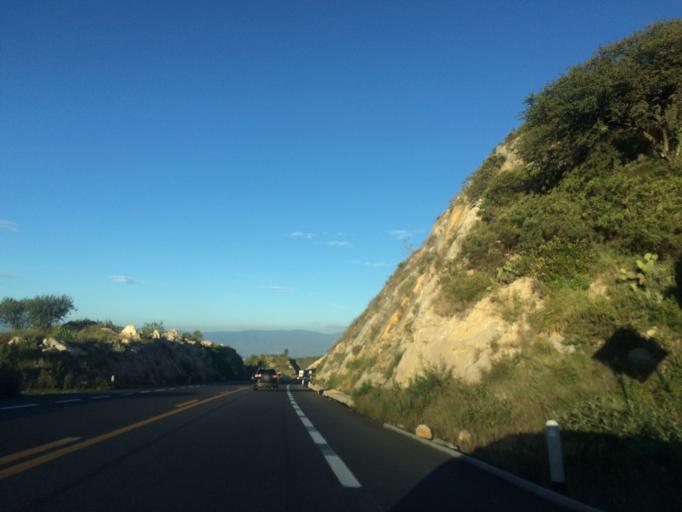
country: MX
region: Puebla
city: Chapuco
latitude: 18.6233
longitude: -97.4658
